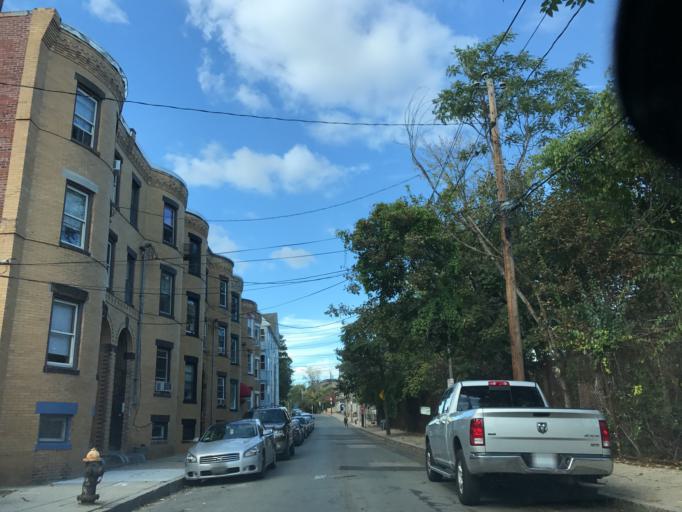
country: US
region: Massachusetts
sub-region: Norfolk County
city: Brookline
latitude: 42.3268
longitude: -71.0892
